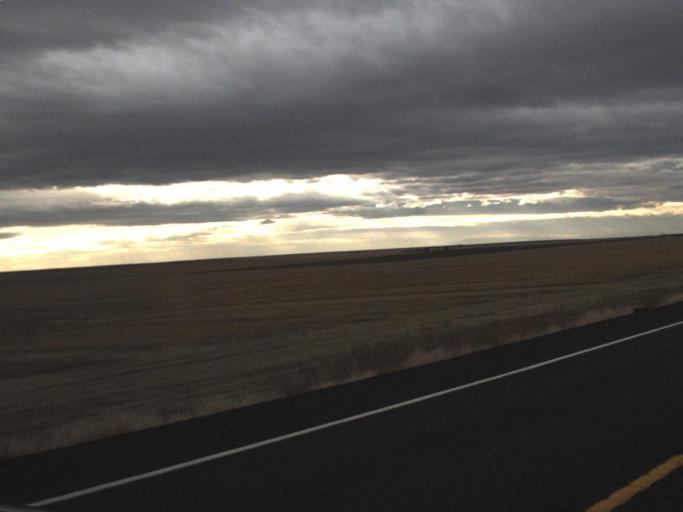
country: US
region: Washington
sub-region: Franklin County
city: Connell
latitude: 46.7945
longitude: -118.6103
